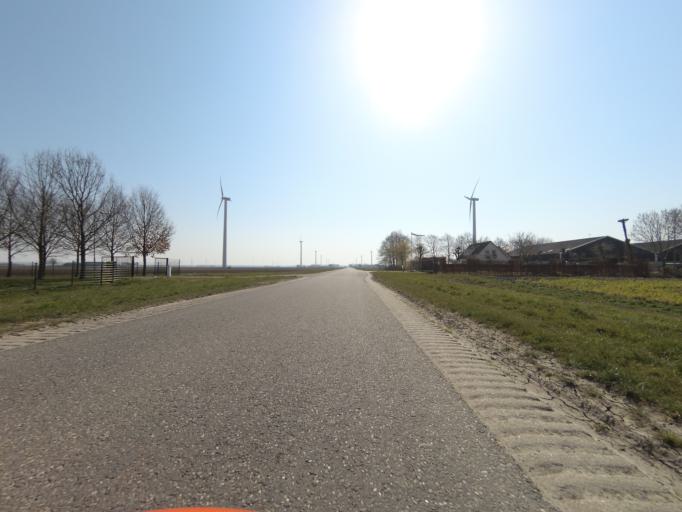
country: NL
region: Utrecht
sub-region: Gemeente Bunschoten
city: Spakenburg
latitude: 52.3519
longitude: 5.3661
